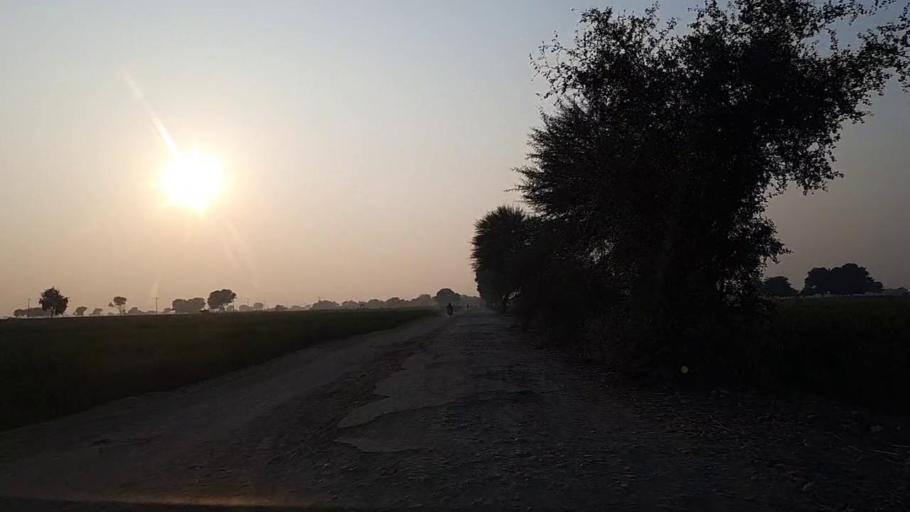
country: PK
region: Sindh
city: Sann
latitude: 26.1948
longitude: 68.0874
